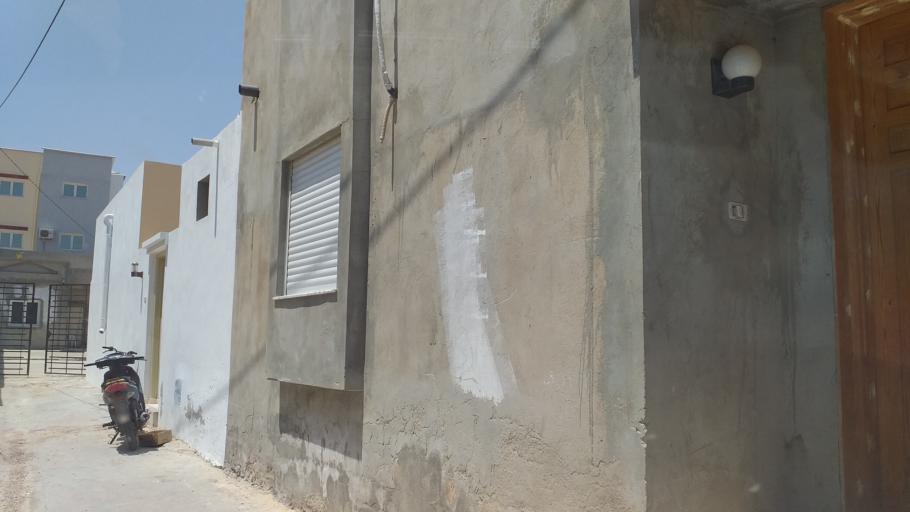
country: TN
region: Qabis
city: Gabes
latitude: 33.9421
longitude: 10.0573
